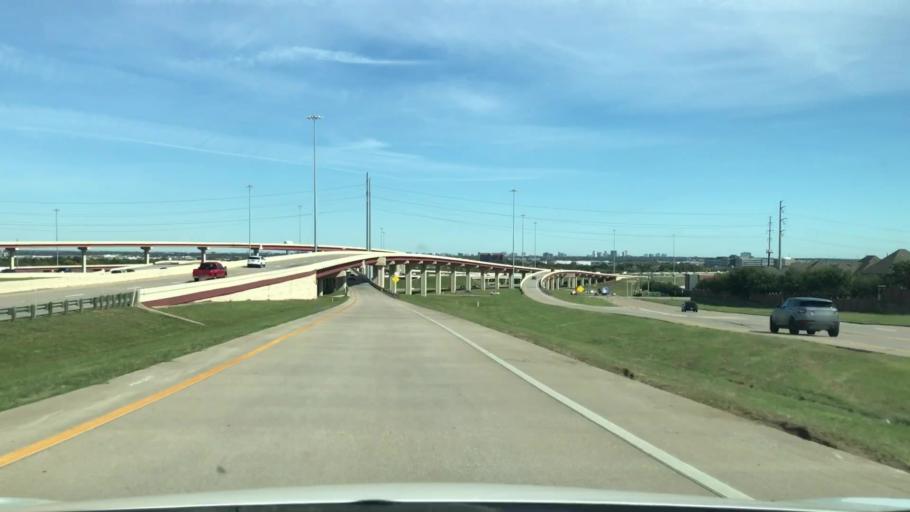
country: US
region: Texas
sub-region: Dallas County
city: Farmers Branch
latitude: 32.9092
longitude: -96.9494
